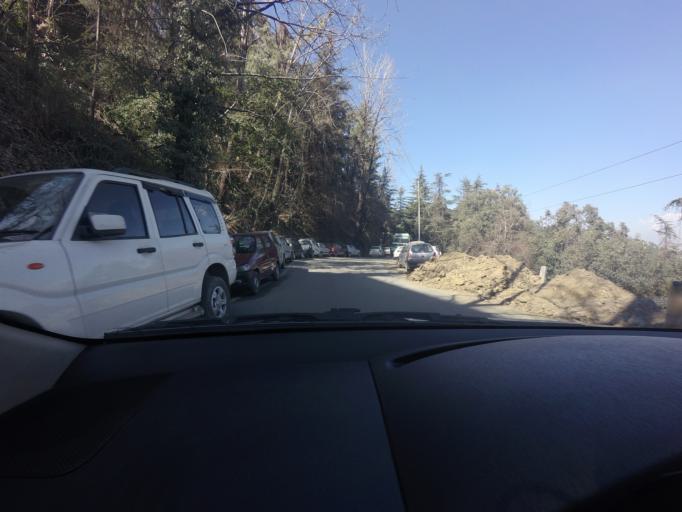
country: IN
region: Himachal Pradesh
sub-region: Shimla
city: Shimla
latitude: 31.1077
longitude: 77.1833
